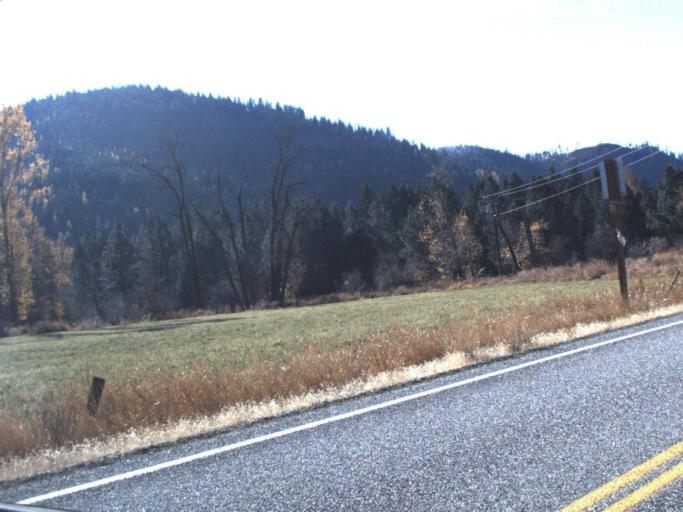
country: CA
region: British Columbia
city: Grand Forks
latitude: 48.9563
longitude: -118.5364
